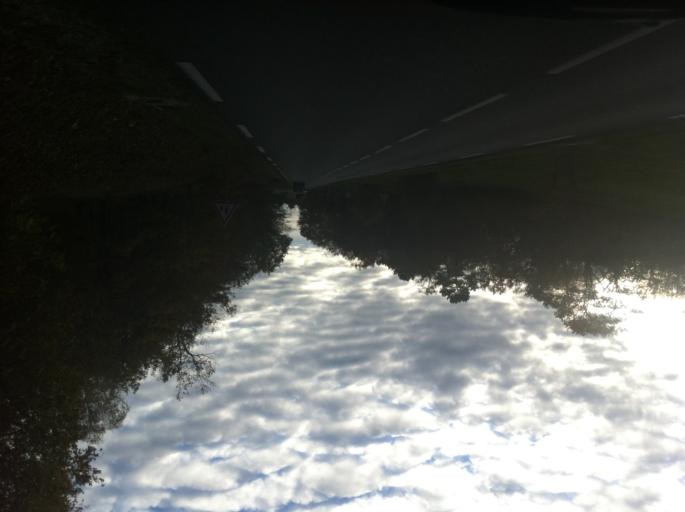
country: FR
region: Aquitaine
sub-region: Departement de la Dordogne
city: Mensignac
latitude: 45.2023
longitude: 0.6112
